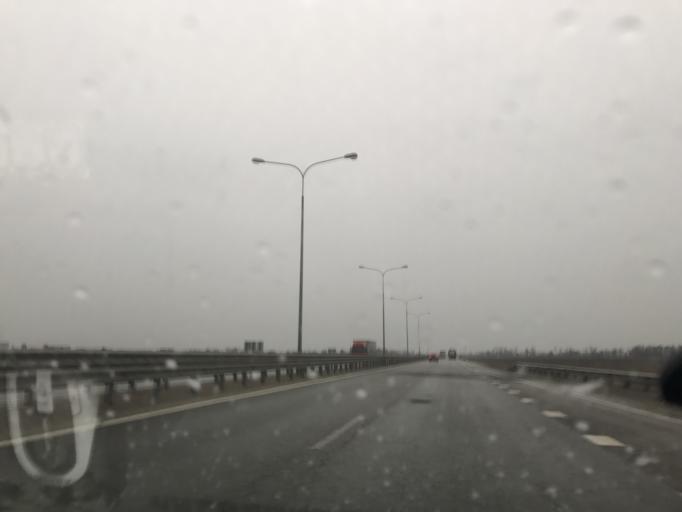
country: RU
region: Krasnodarskiy
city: Krylovskaya
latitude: 46.2885
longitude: 39.8254
